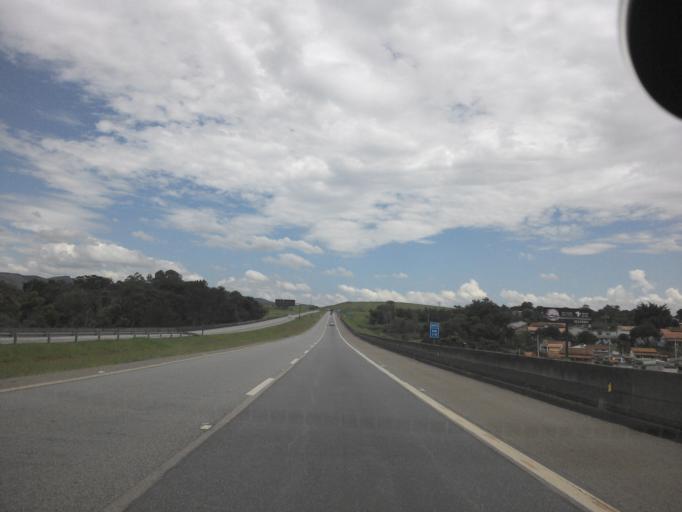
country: BR
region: Sao Paulo
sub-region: Cacapava
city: Cacapava
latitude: -23.1859
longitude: -45.7312
